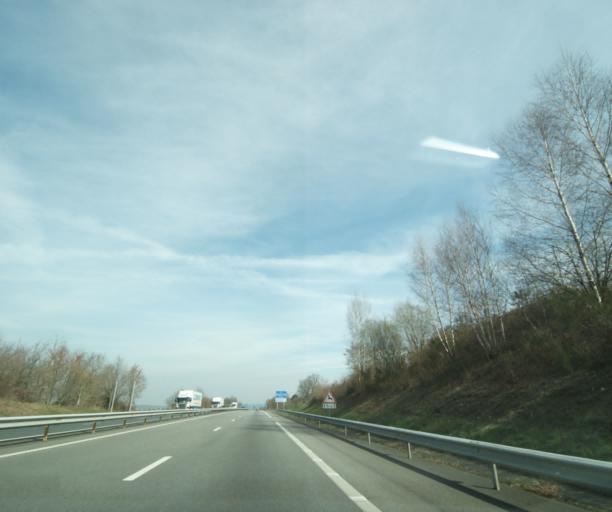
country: FR
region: Limousin
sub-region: Departement de la Correze
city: Uzerche
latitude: 45.4634
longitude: 1.5140
